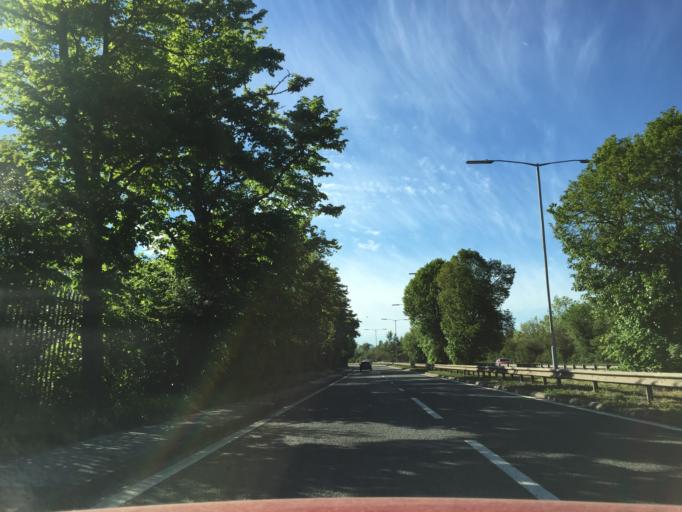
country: GB
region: England
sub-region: Warwickshire
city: Ryton on Dunsmore
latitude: 52.3684
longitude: -1.4429
